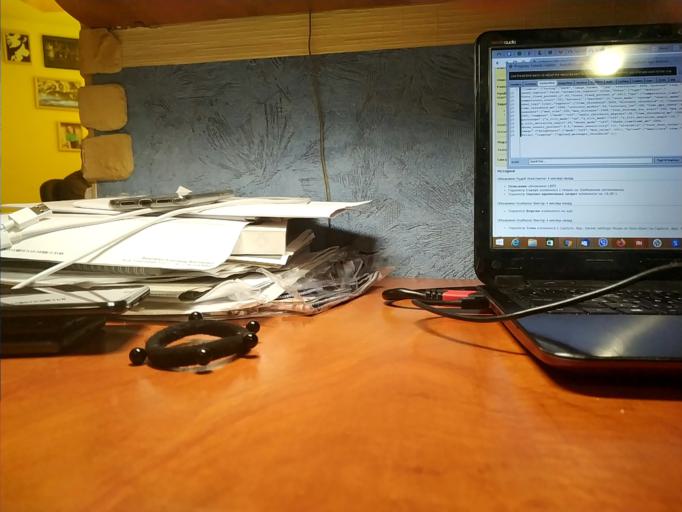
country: RU
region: Vologda
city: Ustyuzhna
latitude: 58.6695
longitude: 36.4220
